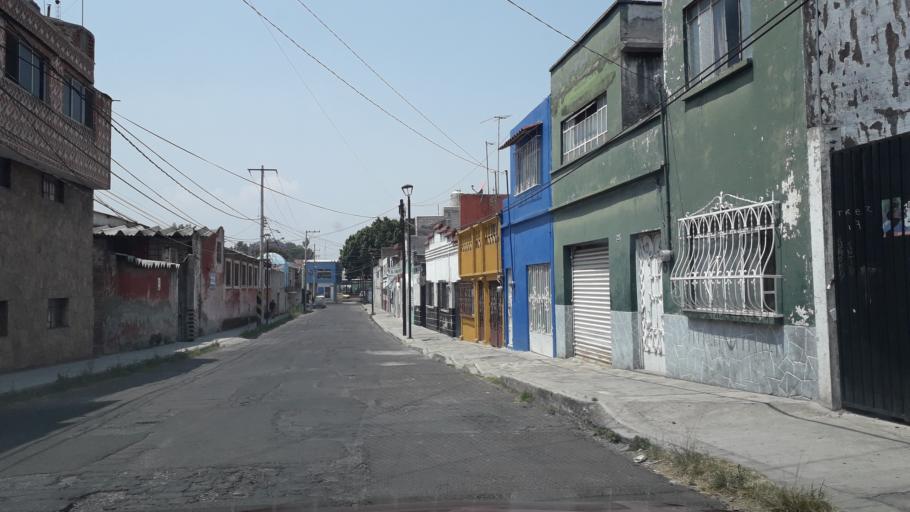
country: MX
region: Puebla
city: Puebla
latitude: 19.0512
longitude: -98.1883
